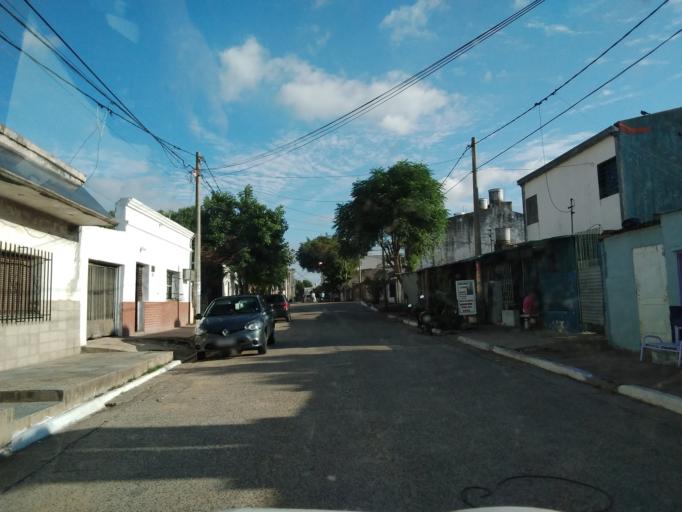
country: AR
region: Corrientes
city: Corrientes
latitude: -27.4593
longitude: -58.8203
